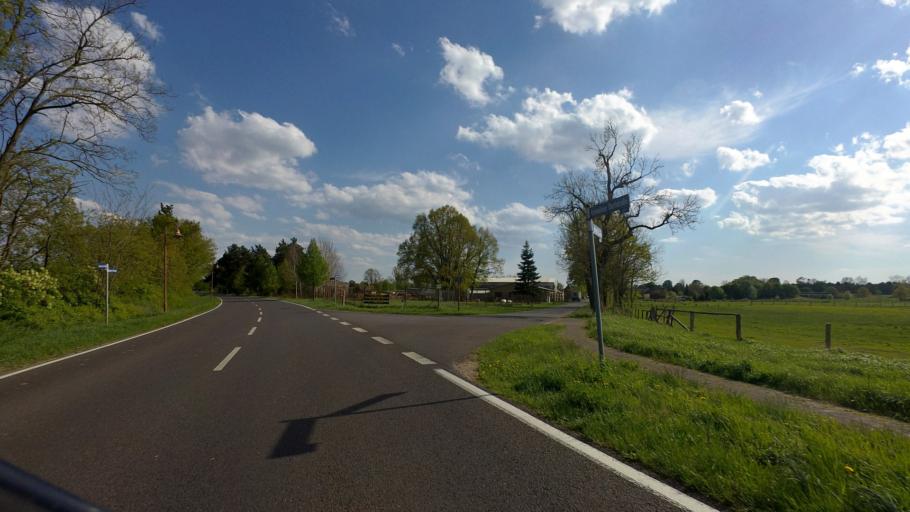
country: DE
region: Brandenburg
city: Zehdenick
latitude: 52.9497
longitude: 13.3824
